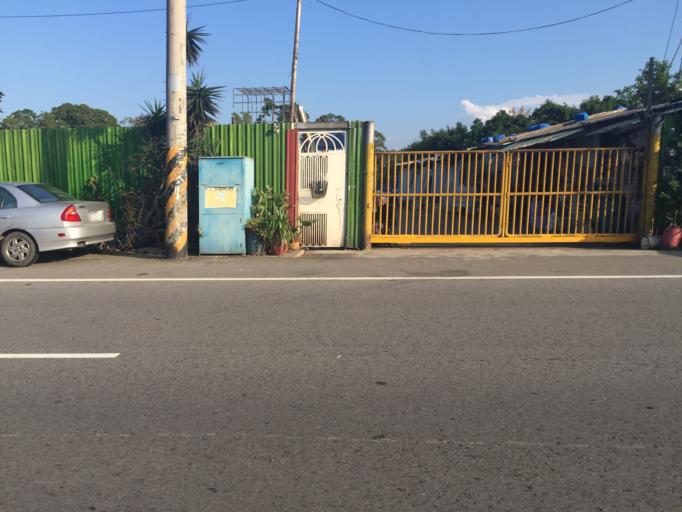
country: TW
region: Taiwan
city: Daxi
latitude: 24.9202
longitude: 121.2551
